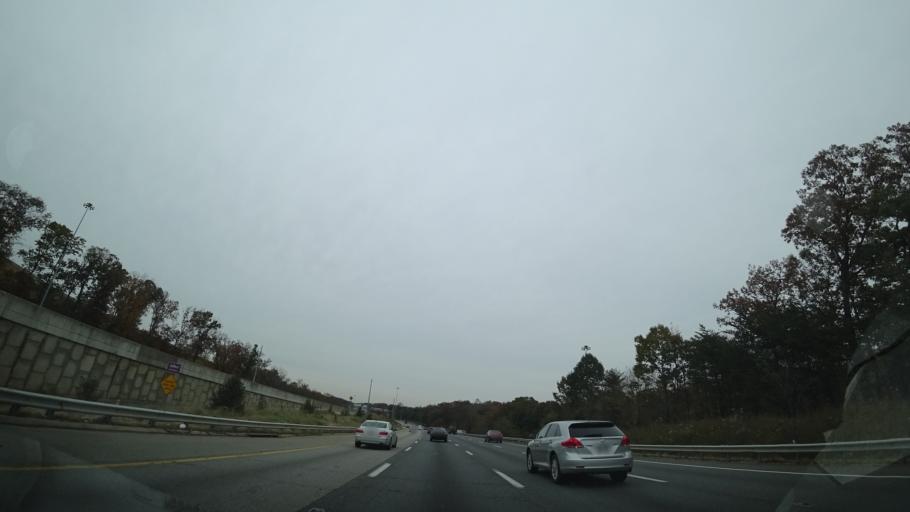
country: US
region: Virginia
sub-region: Fairfax County
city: Lorton
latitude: 38.6811
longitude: -77.2299
